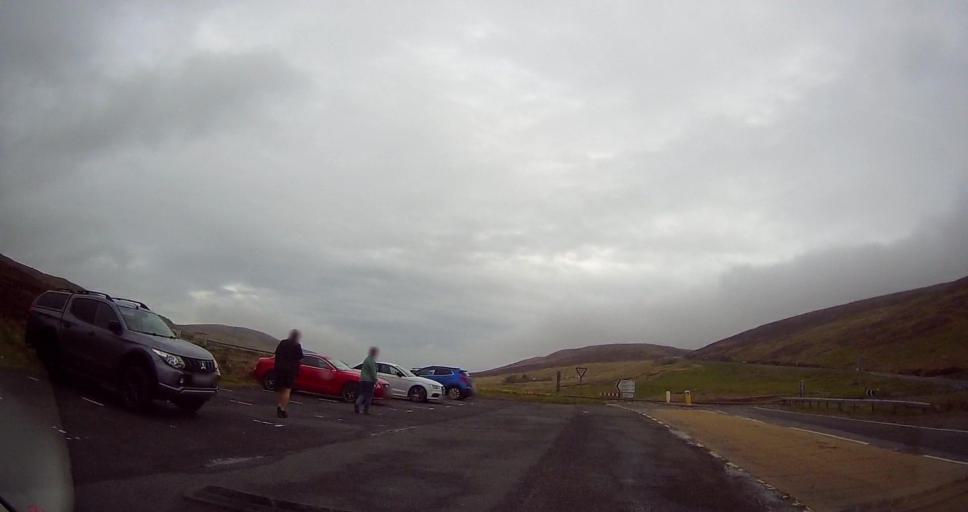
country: GB
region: Scotland
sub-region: Shetland Islands
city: Lerwick
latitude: 60.1602
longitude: -1.2272
